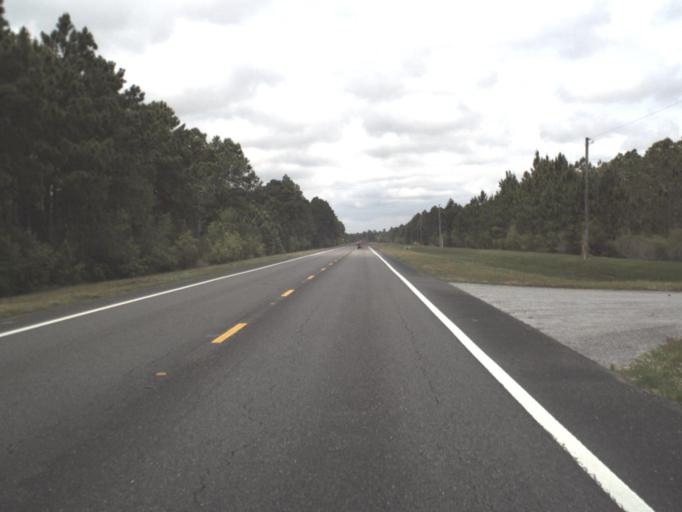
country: US
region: Florida
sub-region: Santa Rosa County
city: Bagdad
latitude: 30.4940
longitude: -87.0804
